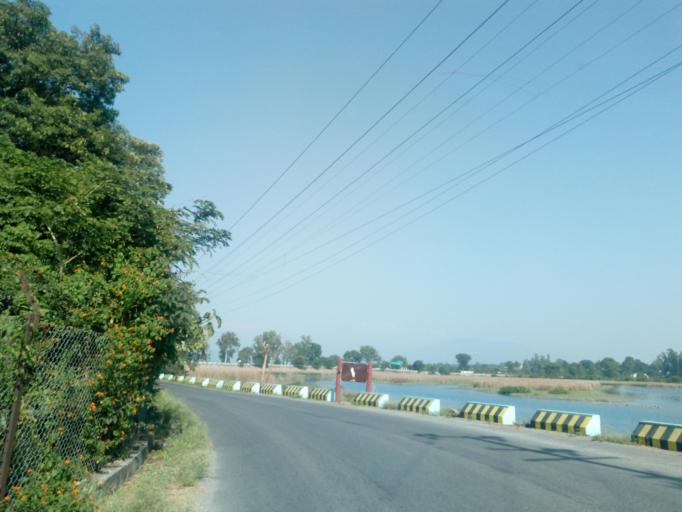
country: IN
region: Himachal Pradesh
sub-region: Sirmaur
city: Paonta Sahib
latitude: 30.4401
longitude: 77.6719
